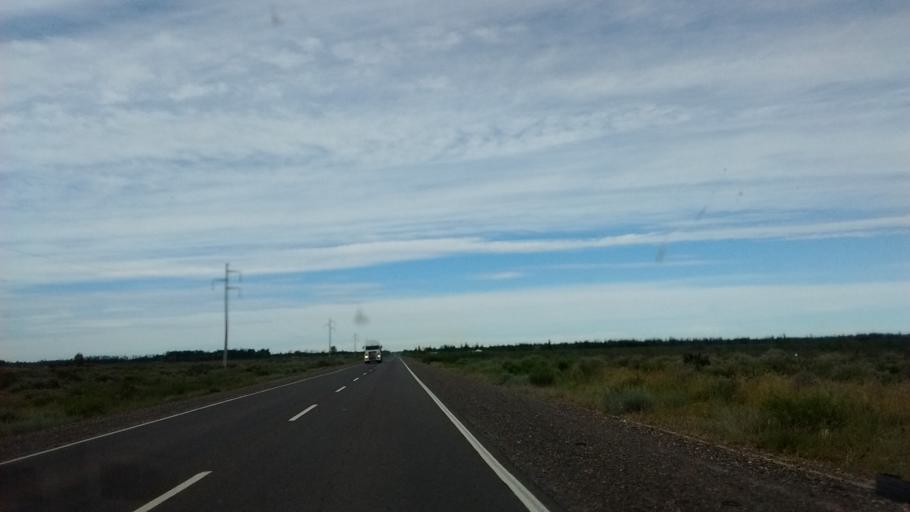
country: AR
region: Rio Negro
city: Contraalmirante Cordero
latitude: -38.6529
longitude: -68.1395
